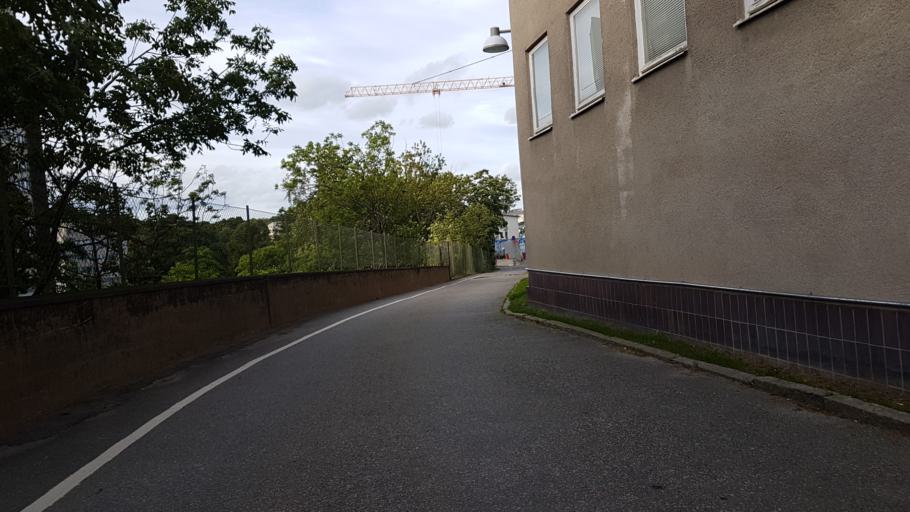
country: SE
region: Stockholm
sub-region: Stockholms Kommun
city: Arsta
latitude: 59.3091
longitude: 18.0512
